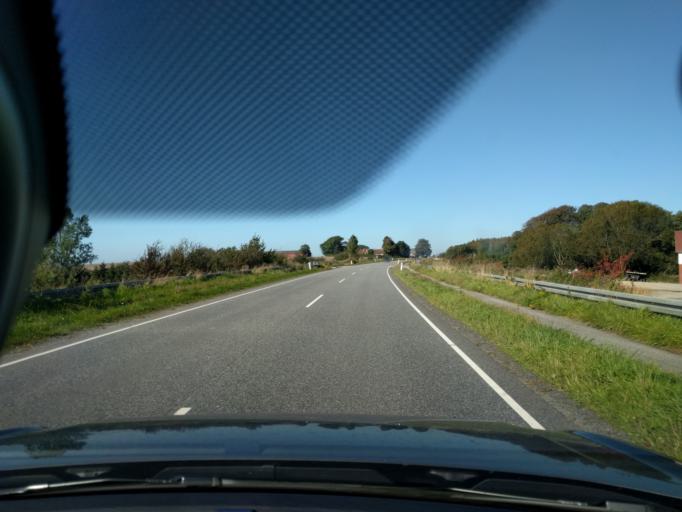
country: DK
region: North Denmark
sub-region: Vesthimmerland Kommune
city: Aars
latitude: 56.7479
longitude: 9.5893
